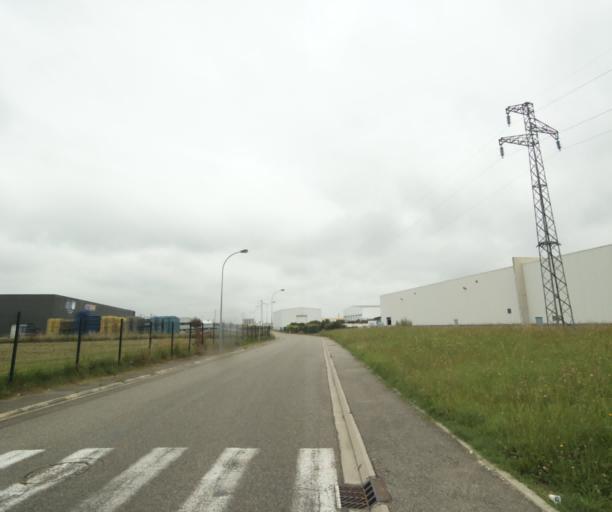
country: FR
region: Midi-Pyrenees
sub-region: Departement du Tarn-et-Garonne
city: Bressols
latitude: 43.9776
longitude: 1.3256
